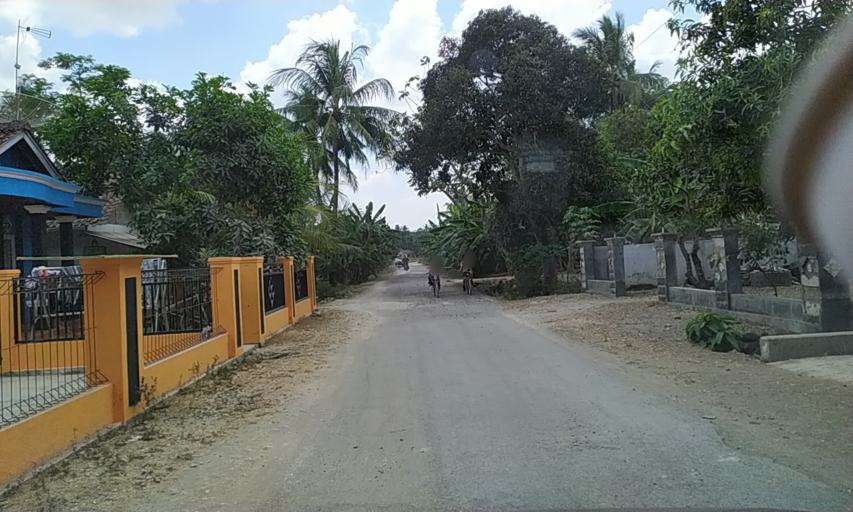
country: ID
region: Central Java
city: Rawaapu
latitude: -7.6288
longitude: 108.7661
